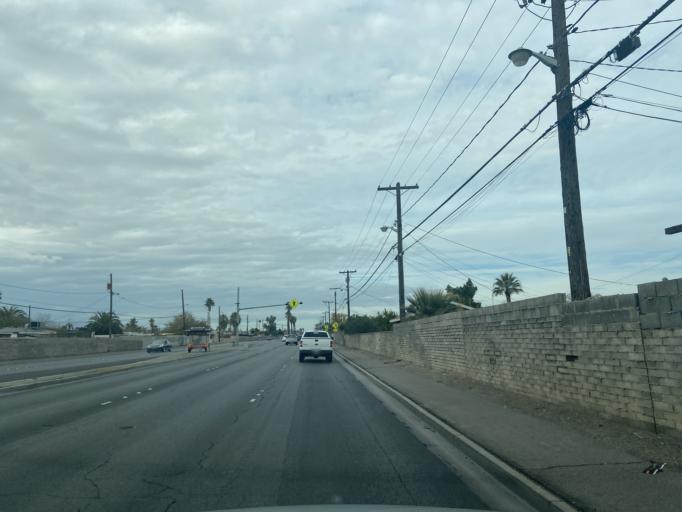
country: US
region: Nevada
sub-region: Clark County
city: Las Vegas
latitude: 36.1842
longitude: -115.1818
